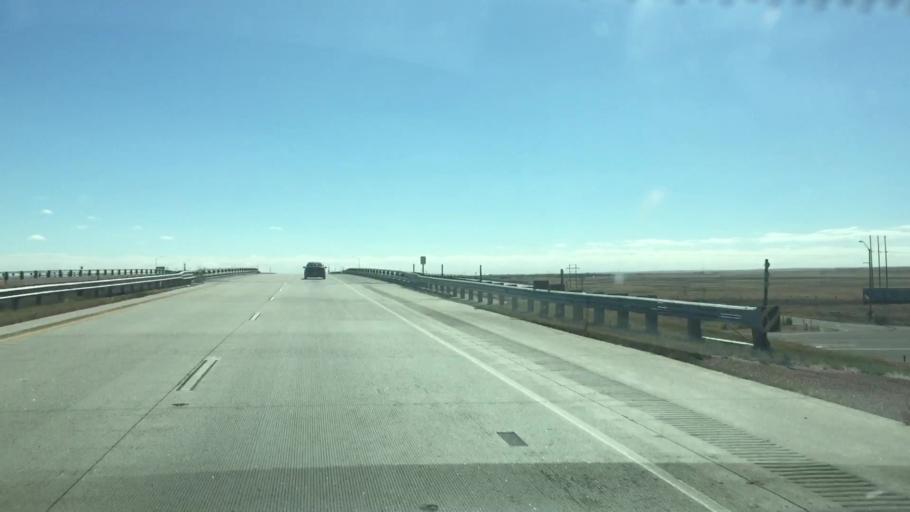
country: US
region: Colorado
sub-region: Lincoln County
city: Limon
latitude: 39.2652
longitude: -103.6692
